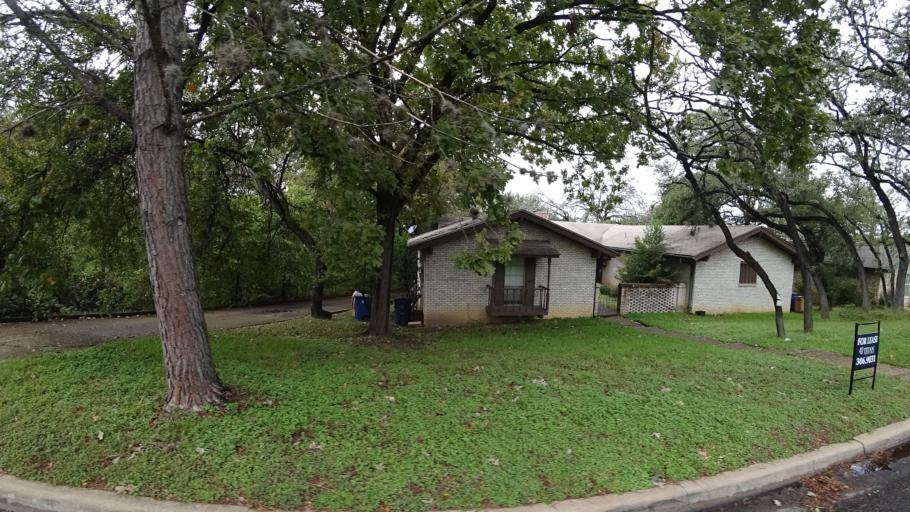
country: US
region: Texas
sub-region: Travis County
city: Rollingwood
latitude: 30.2516
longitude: -97.7794
